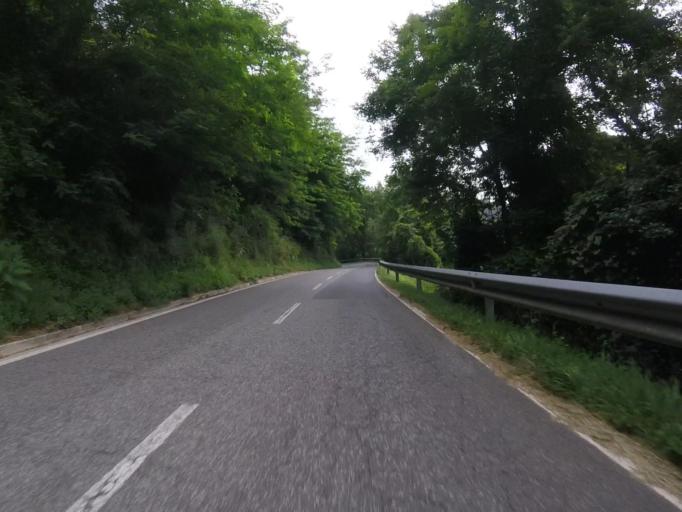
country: ES
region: Navarre
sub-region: Provincia de Navarra
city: Zubieta
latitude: 43.1222
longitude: -1.7533
